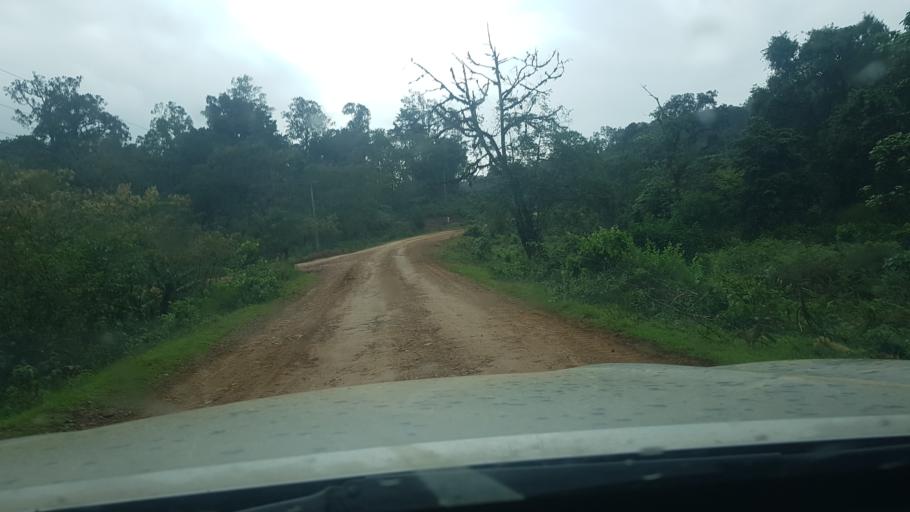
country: ET
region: Oromiya
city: Gore
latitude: 7.8772
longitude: 35.4830
